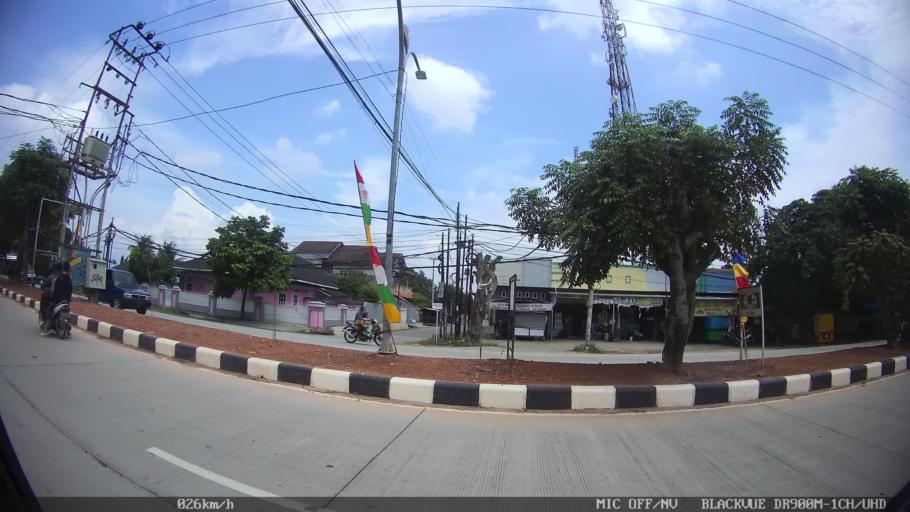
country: ID
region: Lampung
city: Kedaton
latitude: -5.3652
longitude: 105.3017
